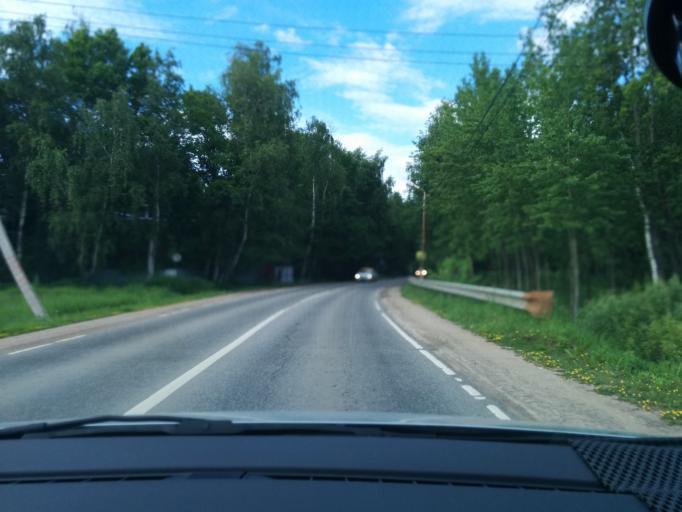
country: RU
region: Moskovskaya
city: Lugovaya
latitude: 56.0351
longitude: 37.4688
